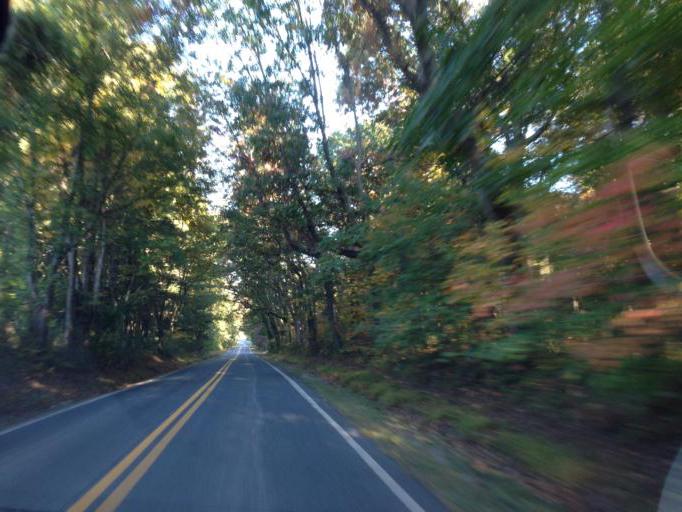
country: US
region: Maryland
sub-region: Carroll County
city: Sykesville
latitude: 39.3328
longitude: -76.9957
